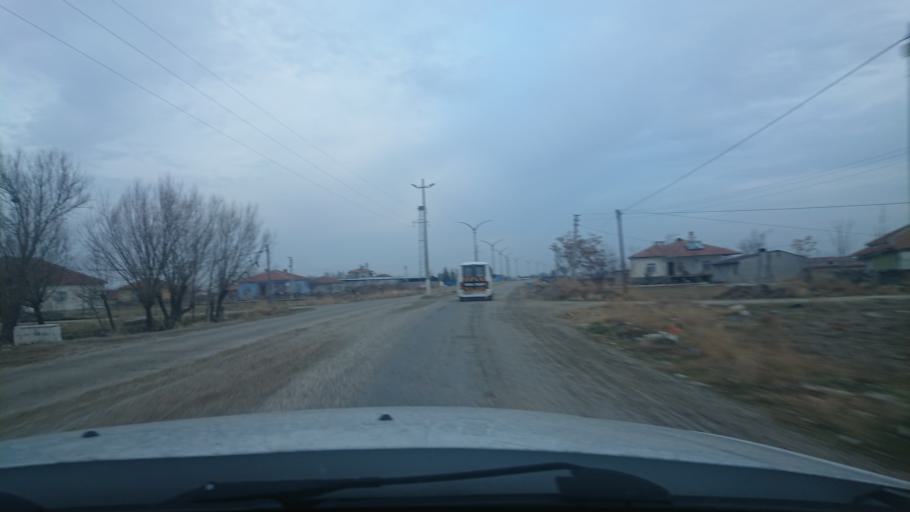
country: TR
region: Aksaray
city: Yesilova
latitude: 38.4180
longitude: 33.8354
